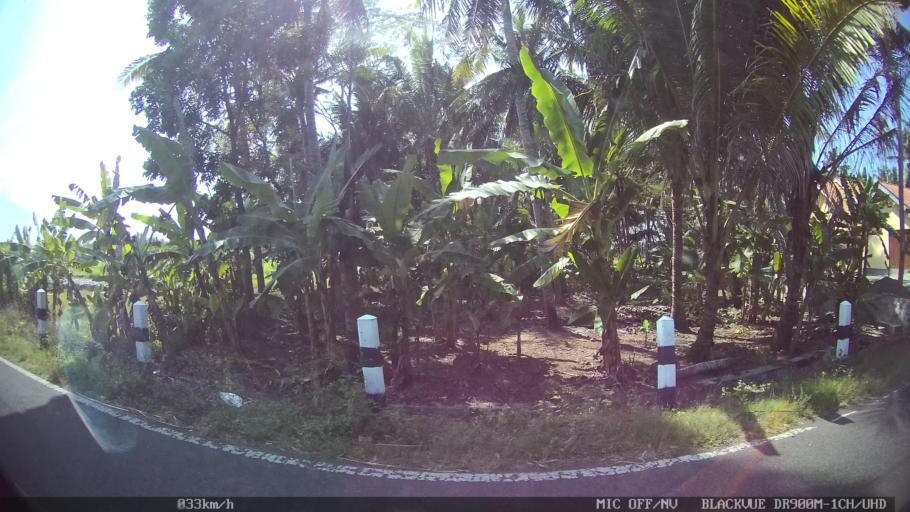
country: ID
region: Daerah Istimewa Yogyakarta
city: Srandakan
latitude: -7.9308
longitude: 110.1559
